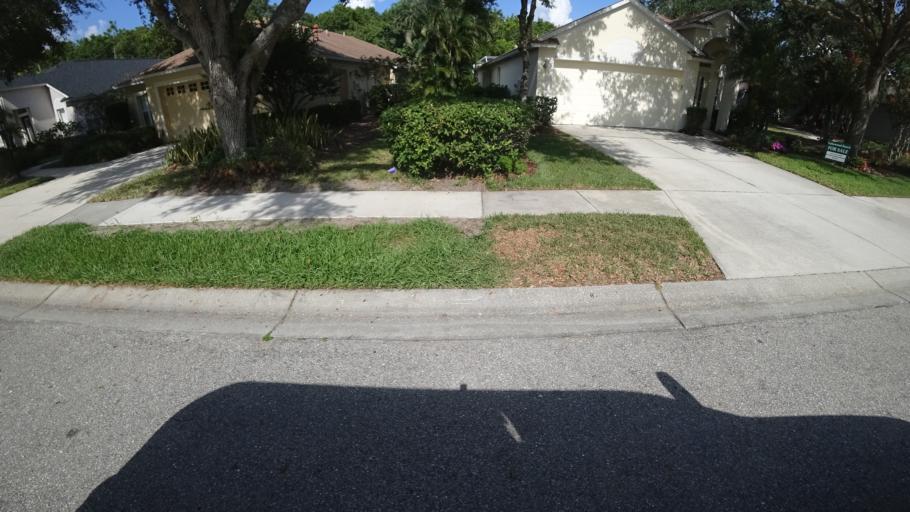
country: US
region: Florida
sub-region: Sarasota County
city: The Meadows
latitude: 27.4296
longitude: -82.4234
